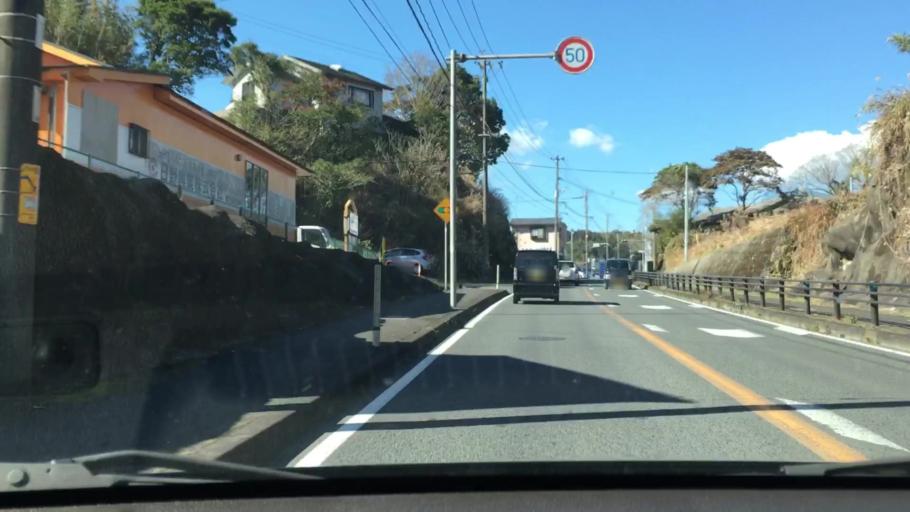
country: JP
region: Kagoshima
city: Ijuin
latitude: 31.6604
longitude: 130.4929
